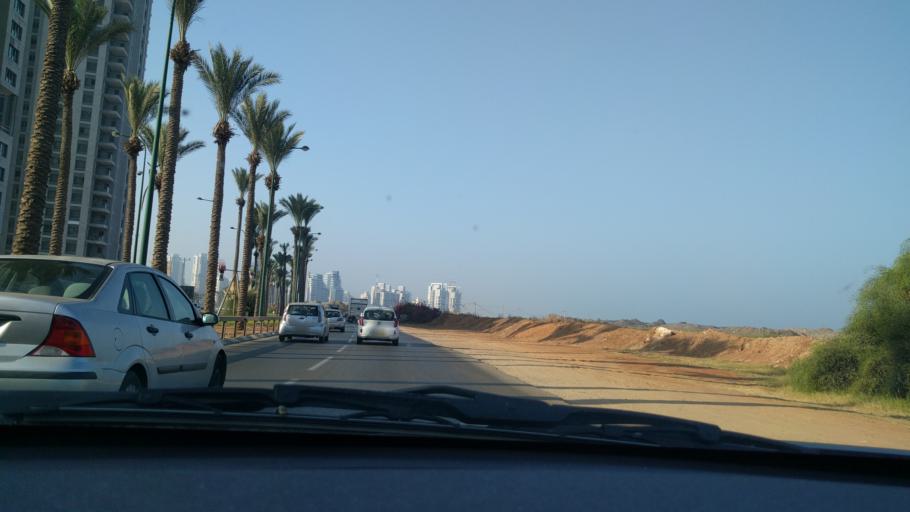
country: IL
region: Central District
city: Netanya
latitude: 32.2936
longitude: 34.8424
